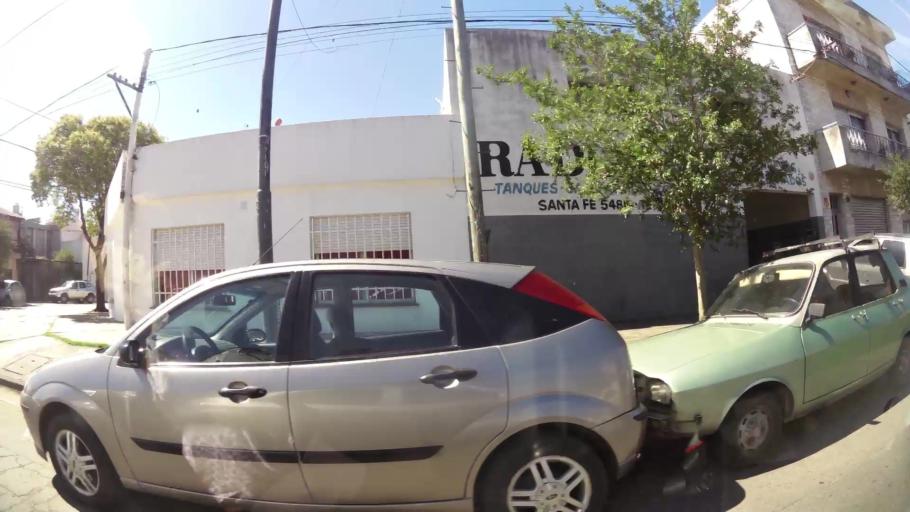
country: AR
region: Santa Fe
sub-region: Departamento de Rosario
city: Rosario
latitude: -32.9353
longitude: -60.6973
